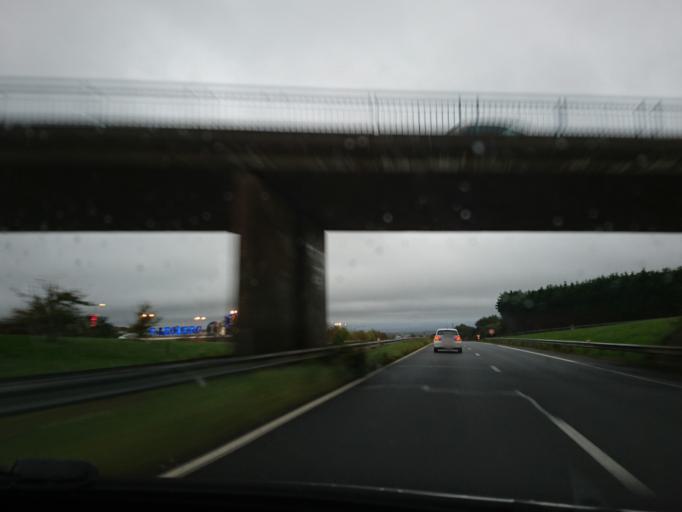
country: FR
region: Brittany
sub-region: Departement du Finistere
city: Plougastel-Daoulas
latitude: 48.3828
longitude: -4.3494
